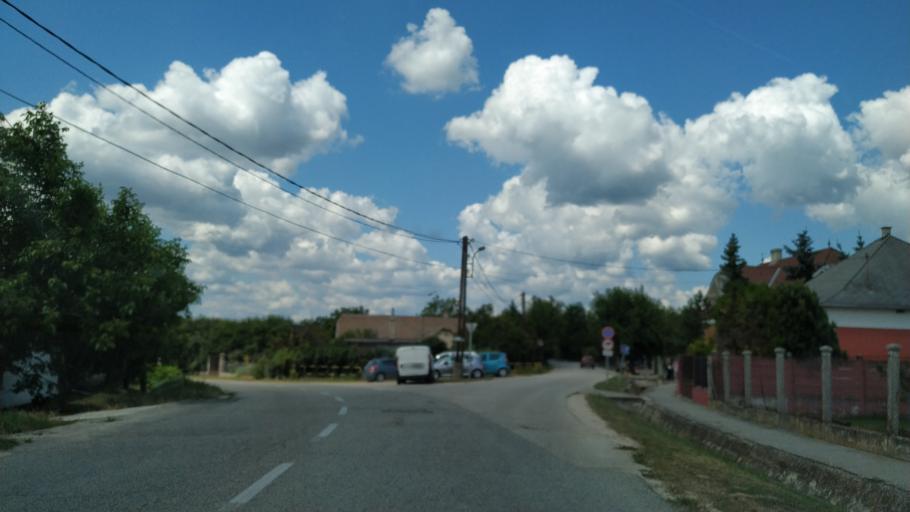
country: HU
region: Veszprem
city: Varpalota
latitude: 47.2004
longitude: 18.1758
